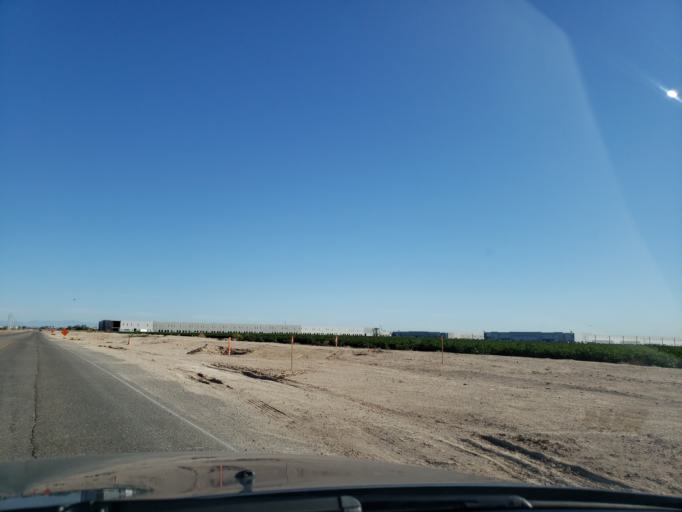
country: US
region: Arizona
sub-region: Maricopa County
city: Goodyear
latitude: 33.4360
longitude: -112.3756
